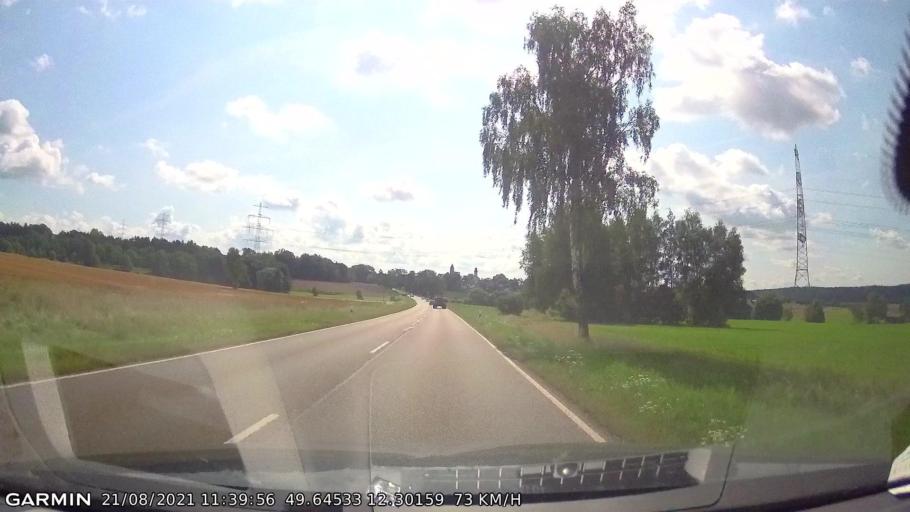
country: DE
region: Bavaria
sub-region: Upper Palatinate
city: Waldthurn
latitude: 49.6454
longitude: 12.3015
